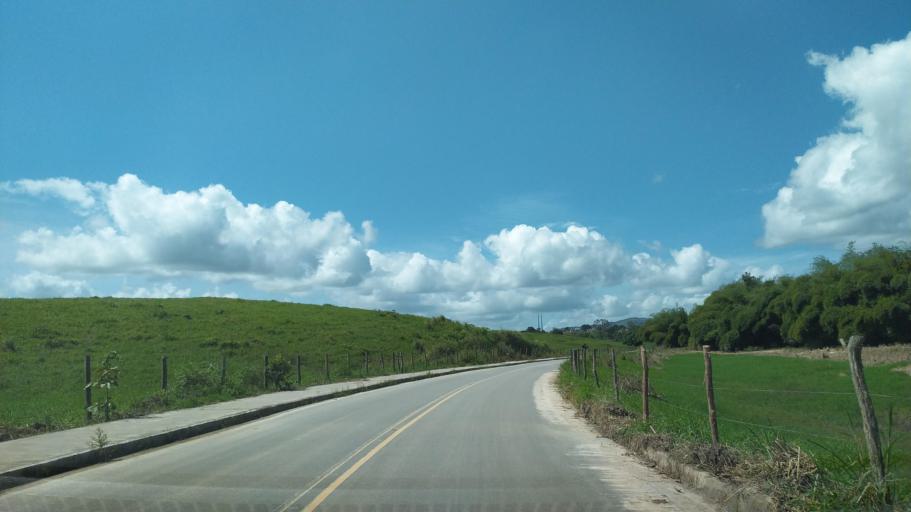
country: BR
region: Alagoas
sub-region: Uniao Dos Palmares
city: Uniao dos Palmares
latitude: -9.1576
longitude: -36.0435
